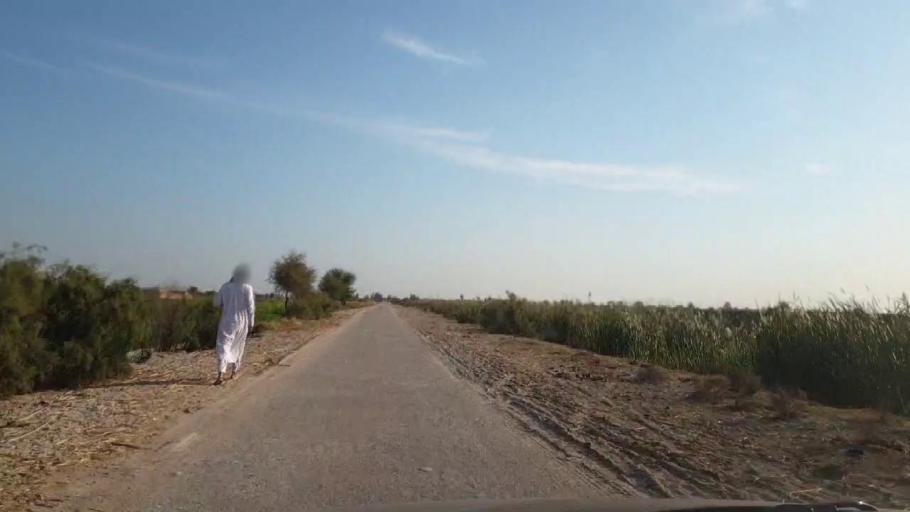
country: PK
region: Sindh
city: Khadro
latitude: 26.2095
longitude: 68.7451
